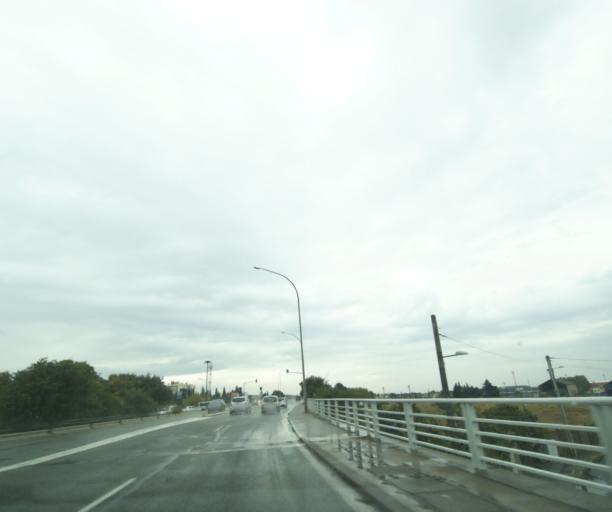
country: FR
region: Languedoc-Roussillon
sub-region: Departement du Gard
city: Rodilhan
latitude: 43.8468
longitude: 4.3963
